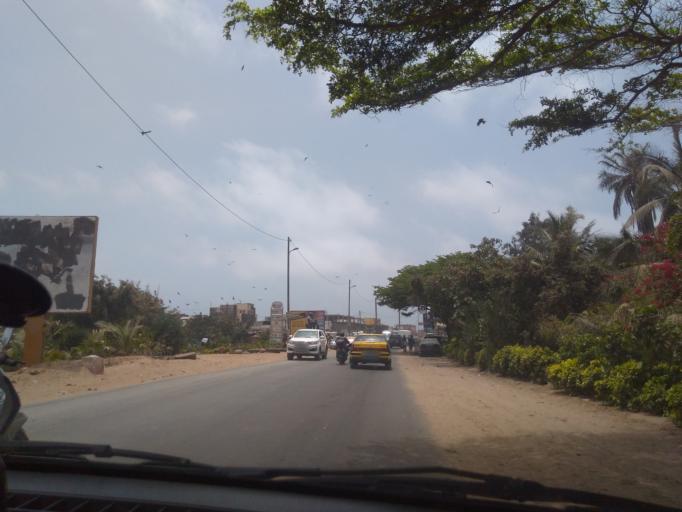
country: SN
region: Dakar
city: Pikine
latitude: 14.7512
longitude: -17.4280
